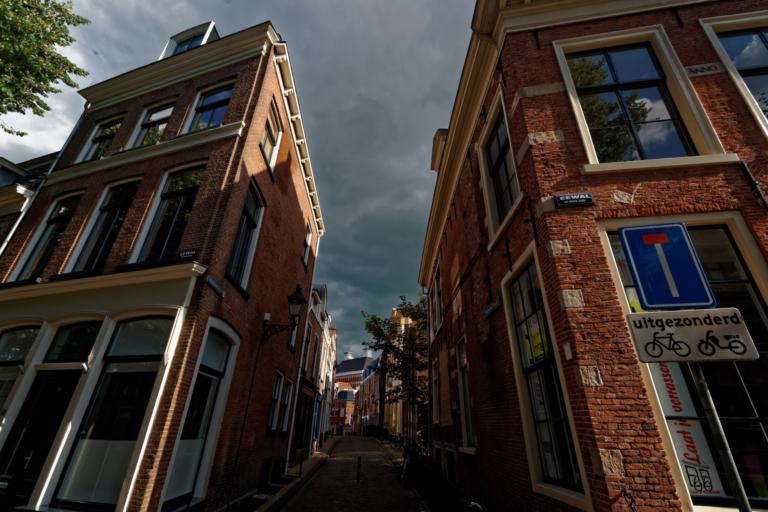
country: NL
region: Friesland
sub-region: Gemeente Leeuwarden
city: Leeuwarden
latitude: 53.2028
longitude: 5.7979
